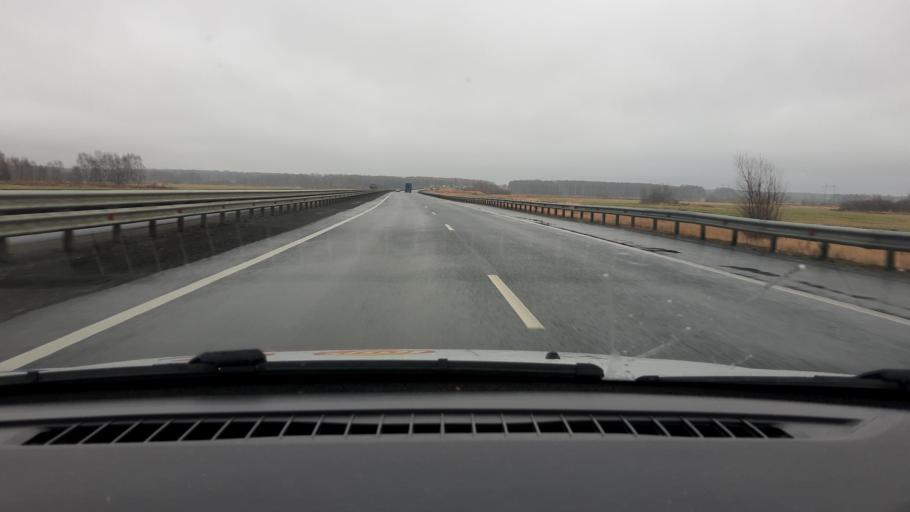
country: RU
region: Nizjnij Novgorod
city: Burevestnik
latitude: 56.1258
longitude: 43.7904
